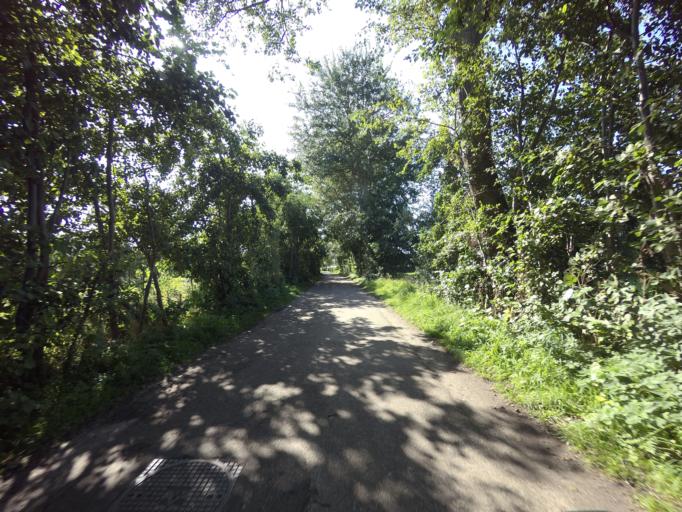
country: NL
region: Friesland
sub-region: Gemeente Terschelling
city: West-Terschelling
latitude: 53.3904
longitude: 5.3074
